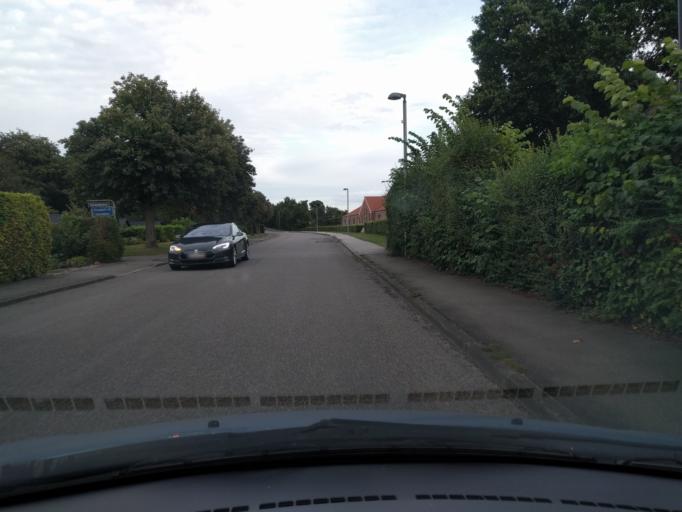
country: DK
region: Zealand
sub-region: Guldborgsund Kommune
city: Stubbekobing
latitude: 54.8913
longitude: 12.0247
